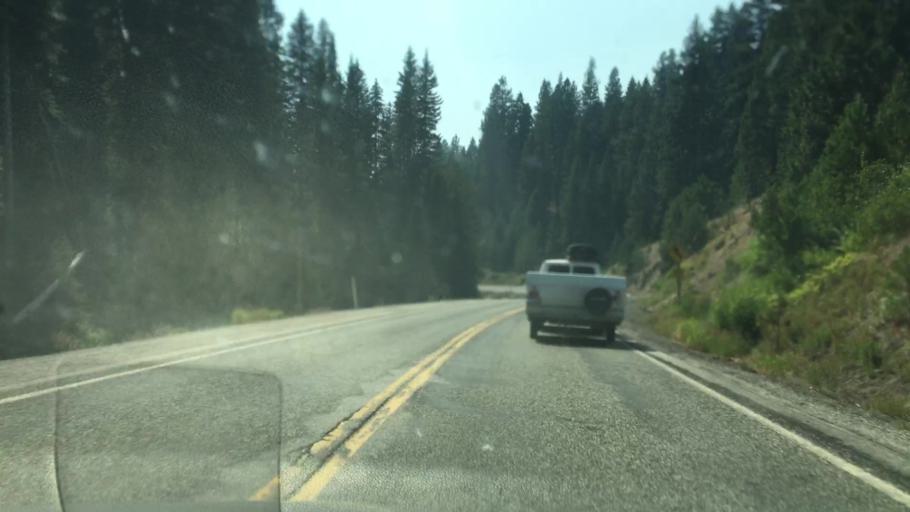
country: US
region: Idaho
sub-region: Valley County
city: Cascade
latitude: 44.3353
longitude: -116.0457
